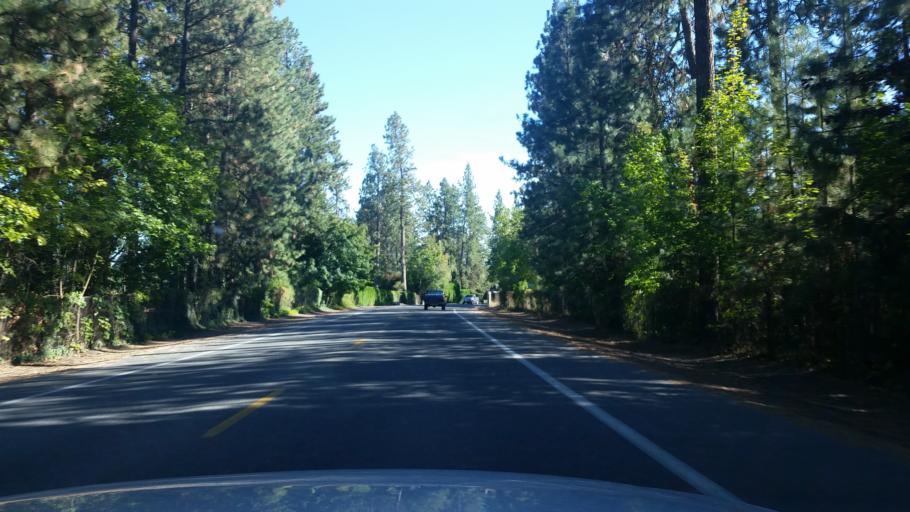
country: US
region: Washington
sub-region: Spokane County
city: Spokane
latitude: 47.6072
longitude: -117.3959
